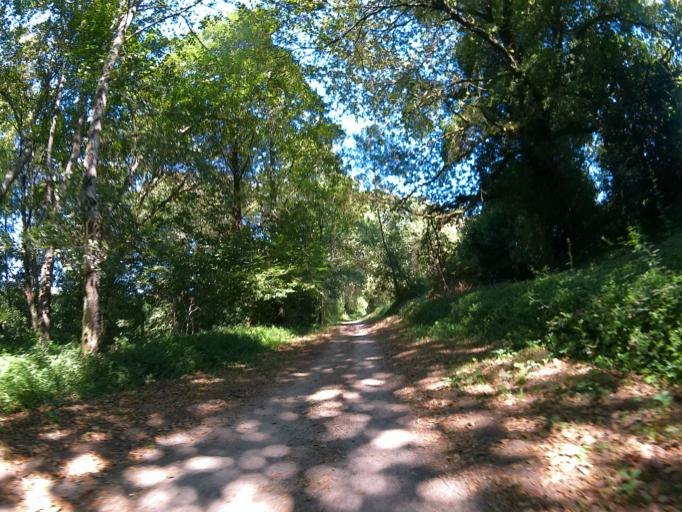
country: PT
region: Viana do Castelo
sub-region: Ponte de Lima
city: Ponte de Lima
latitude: 41.7615
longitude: -8.6010
